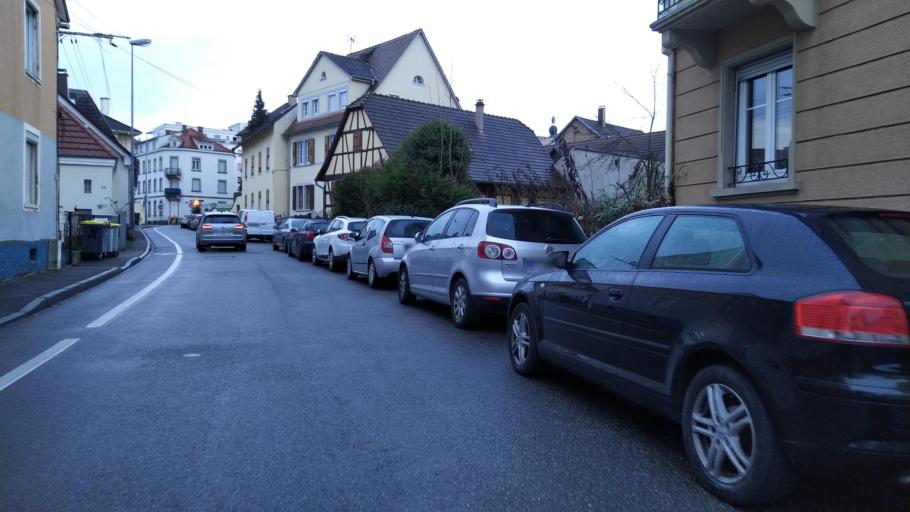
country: FR
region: Alsace
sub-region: Departement du Bas-Rhin
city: Schiltigheim
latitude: 48.6108
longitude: 7.7523
